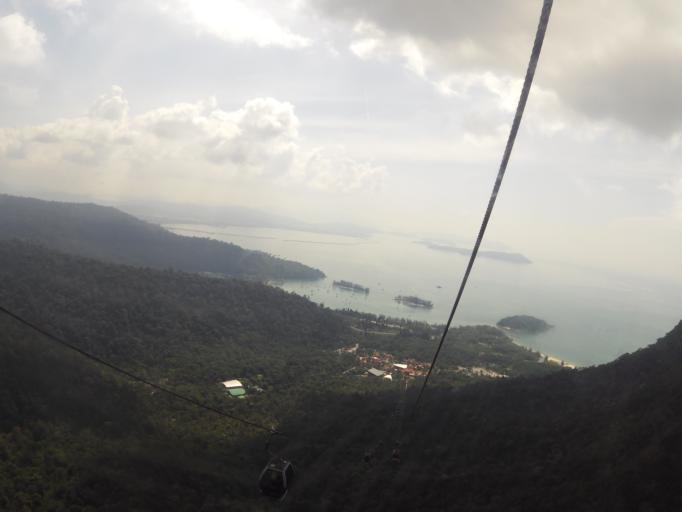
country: MY
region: Kedah
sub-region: Langkawi
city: Kuah
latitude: 6.3825
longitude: 99.6662
